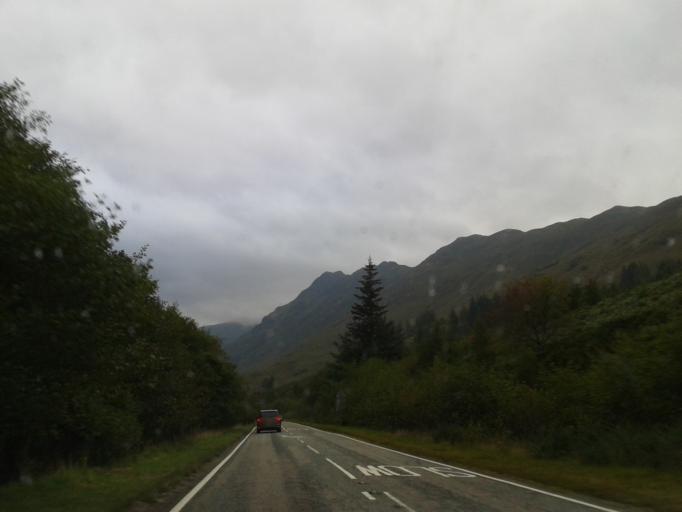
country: GB
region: Scotland
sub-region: Highland
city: Fort William
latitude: 57.2045
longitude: -5.3946
